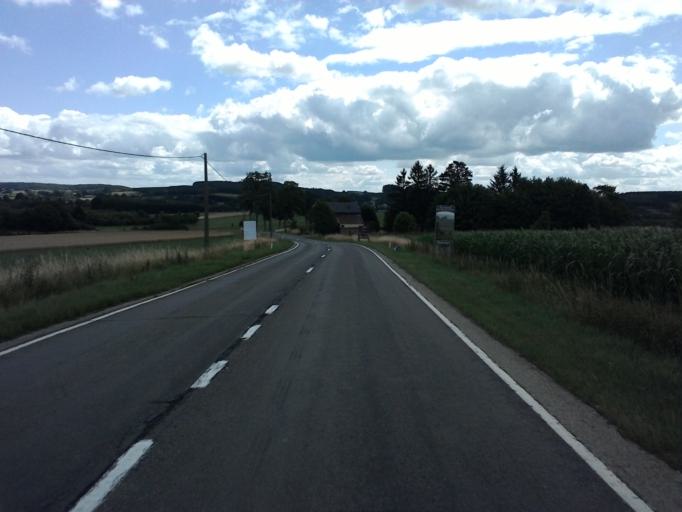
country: BE
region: Wallonia
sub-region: Province du Luxembourg
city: Leglise
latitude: 49.8074
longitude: 5.5223
